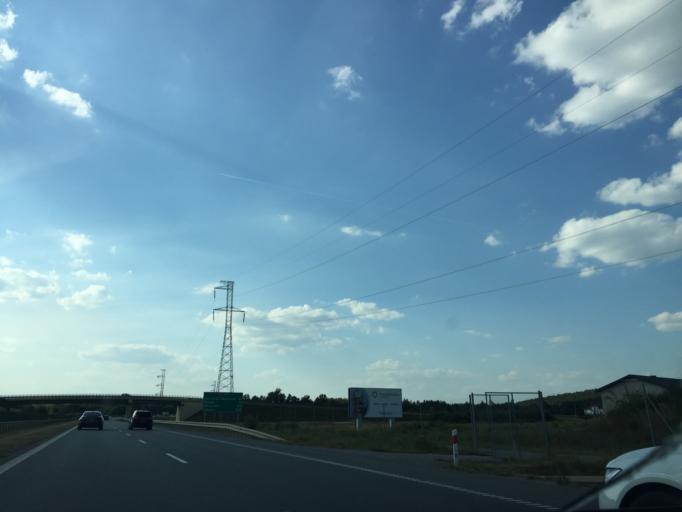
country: PL
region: Swietokrzyskie
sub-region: Powiat kielecki
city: Checiny
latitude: 50.8176
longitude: 20.4767
